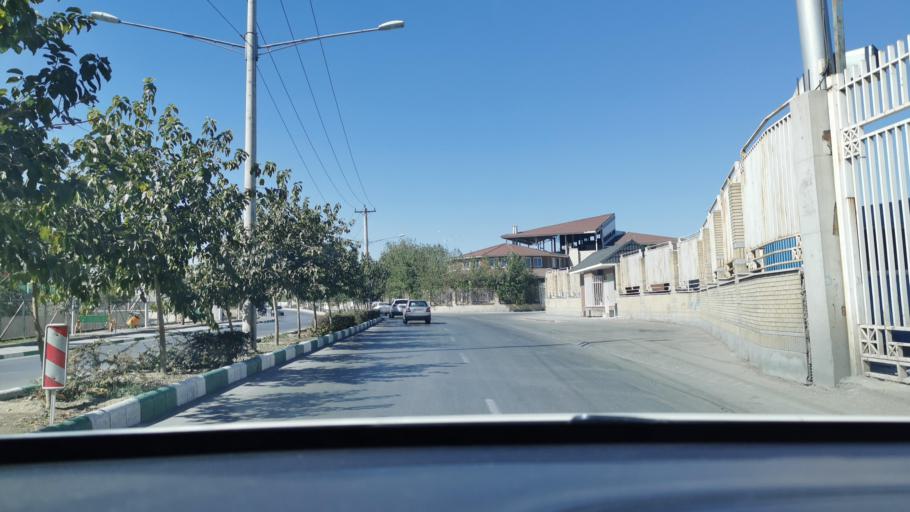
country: IR
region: Razavi Khorasan
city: Mashhad
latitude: 36.3344
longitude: 59.6177
